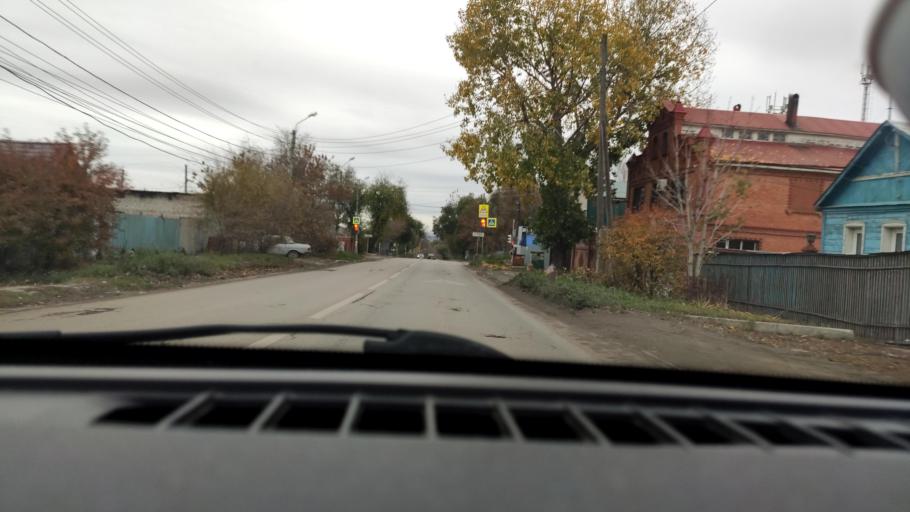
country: RU
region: Samara
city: Samara
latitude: 53.1767
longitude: 50.1700
